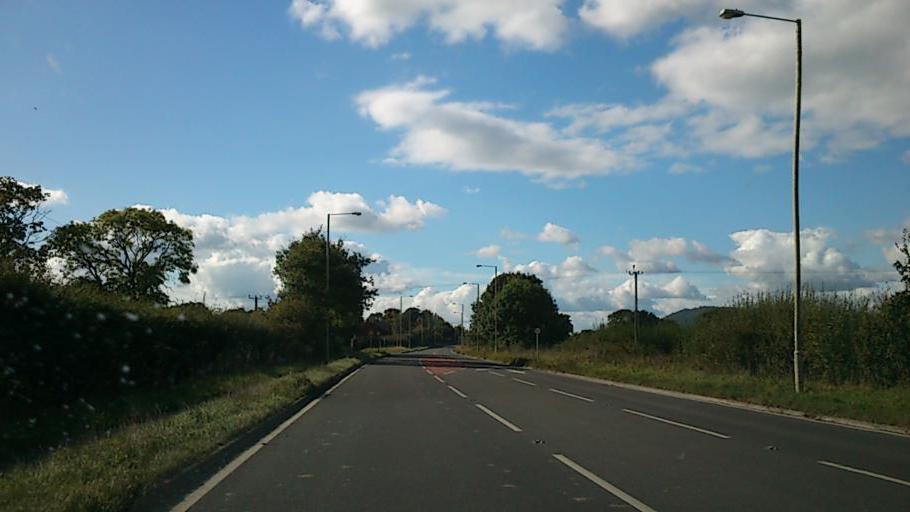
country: GB
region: England
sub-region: Shropshire
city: Westbury
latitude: 52.6988
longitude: -2.9692
